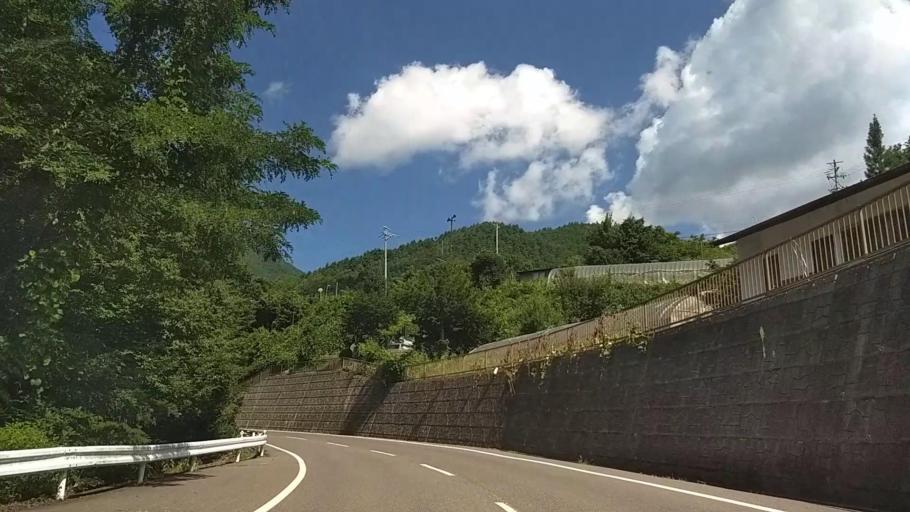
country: JP
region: Nagano
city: Matsumoto
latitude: 36.2164
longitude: 138.0519
